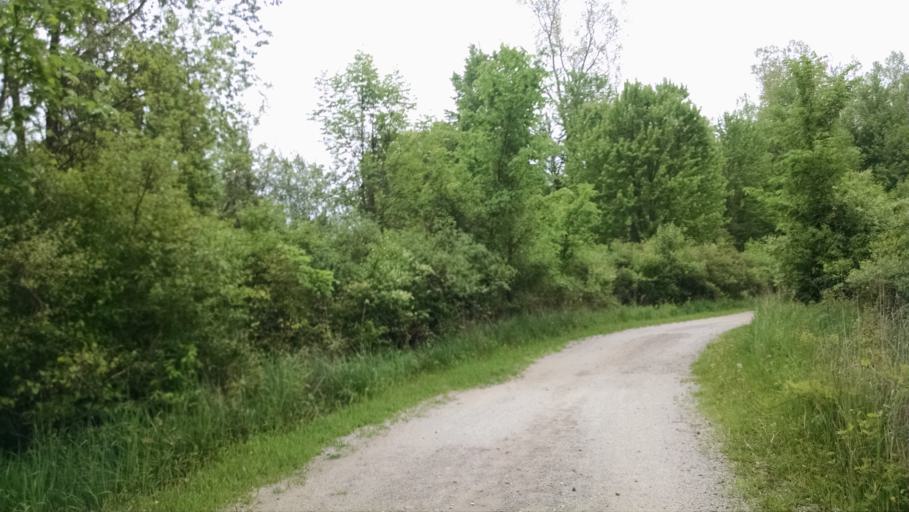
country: US
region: Michigan
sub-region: Eaton County
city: Waverly
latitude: 42.7689
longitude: -84.6399
